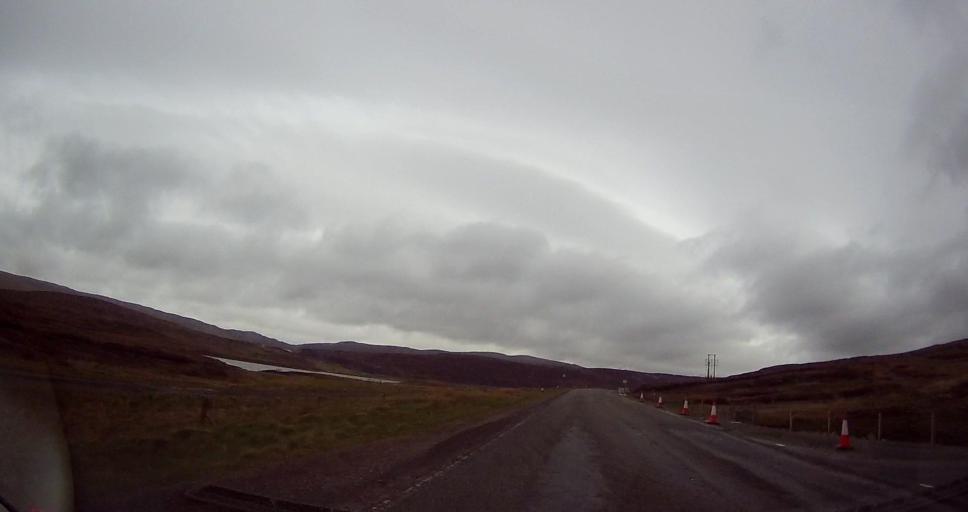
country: GB
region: Scotland
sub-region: Shetland Islands
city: Lerwick
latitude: 60.2724
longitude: -1.2389
